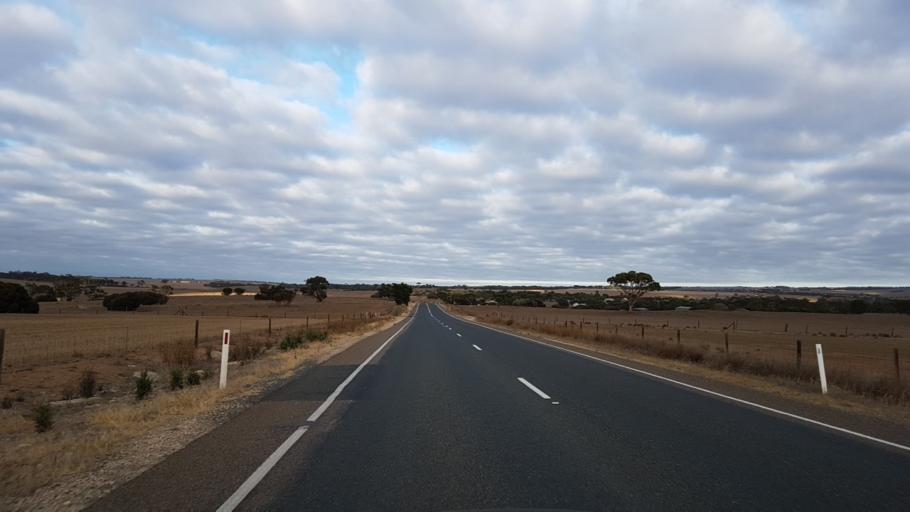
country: AU
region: South Australia
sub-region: Mount Barker
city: Callington
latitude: -35.1999
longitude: 138.9783
